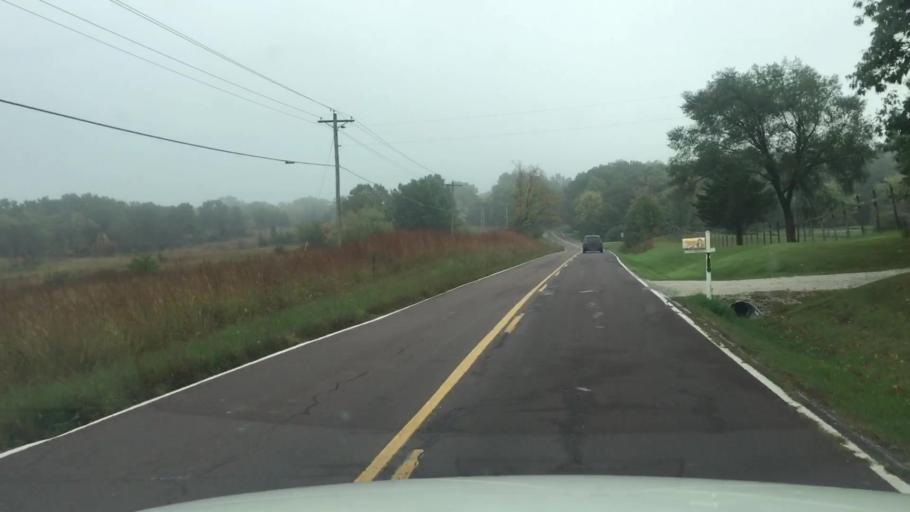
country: US
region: Missouri
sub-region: Boone County
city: Columbia
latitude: 38.8600
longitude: -92.3197
